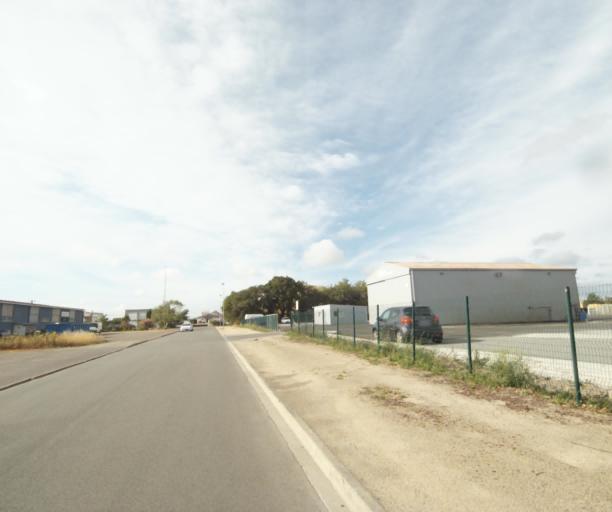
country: FR
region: Pays de la Loire
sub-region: Departement de la Vendee
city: Chateau-d'Olonne
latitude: 46.4888
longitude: -1.7282
